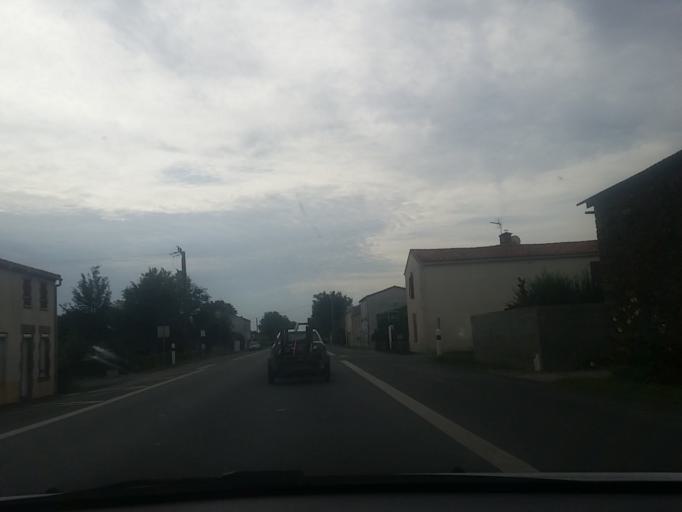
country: FR
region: Pays de la Loire
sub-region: Departement de la Vendee
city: Chavagnes-en-Paillers
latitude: 46.8902
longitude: -1.2208
